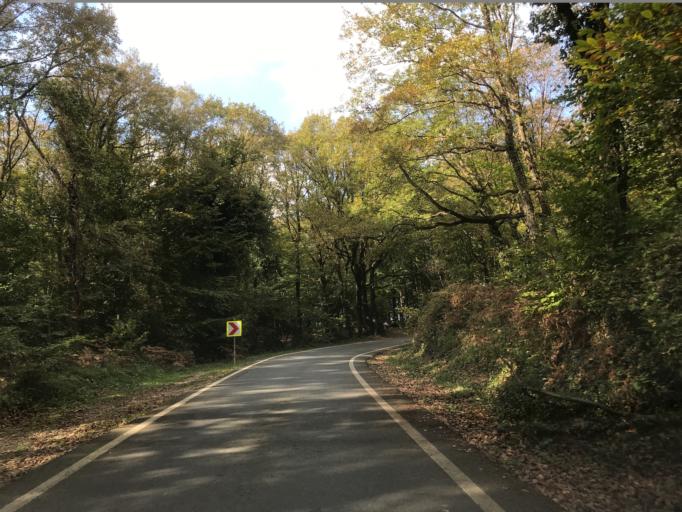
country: TR
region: Istanbul
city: Arikoey
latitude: 41.1846
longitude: 28.9859
